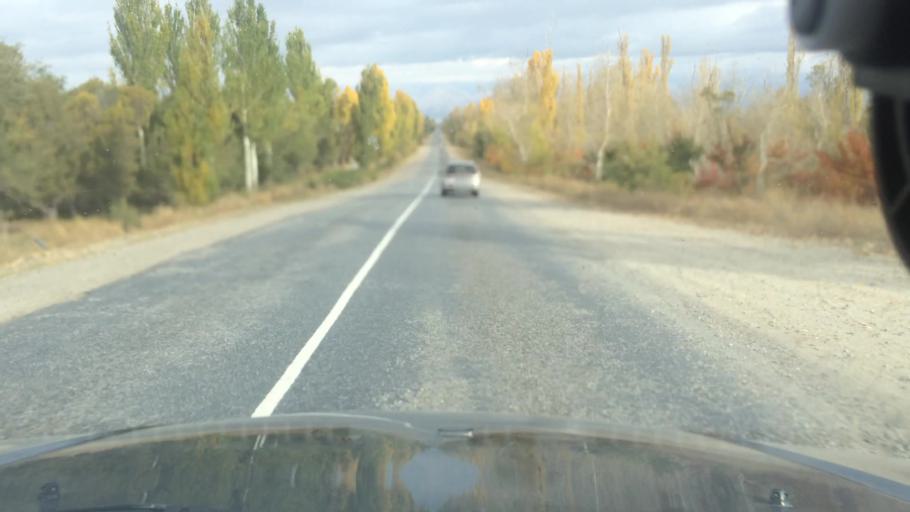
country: KG
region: Ysyk-Koel
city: Tyup
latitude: 42.6110
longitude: 78.3670
